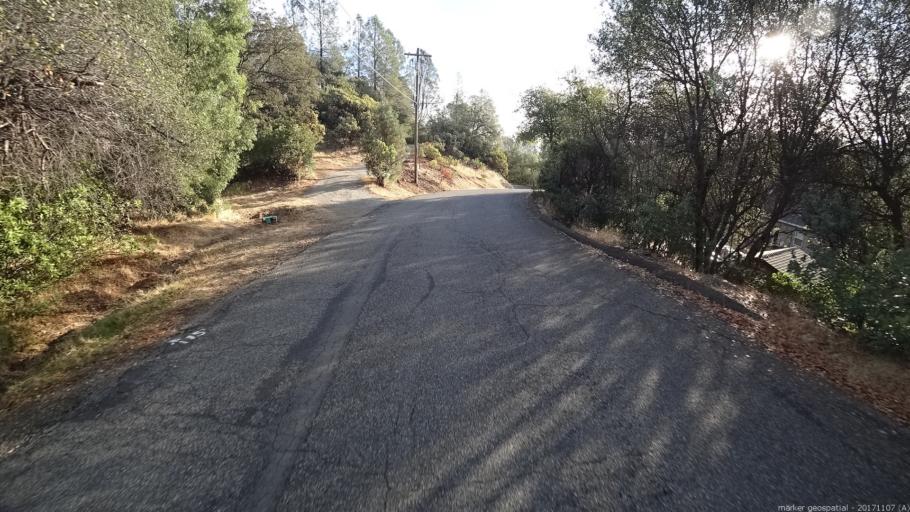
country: US
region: California
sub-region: Shasta County
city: Shasta
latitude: 40.5849
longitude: -122.4679
